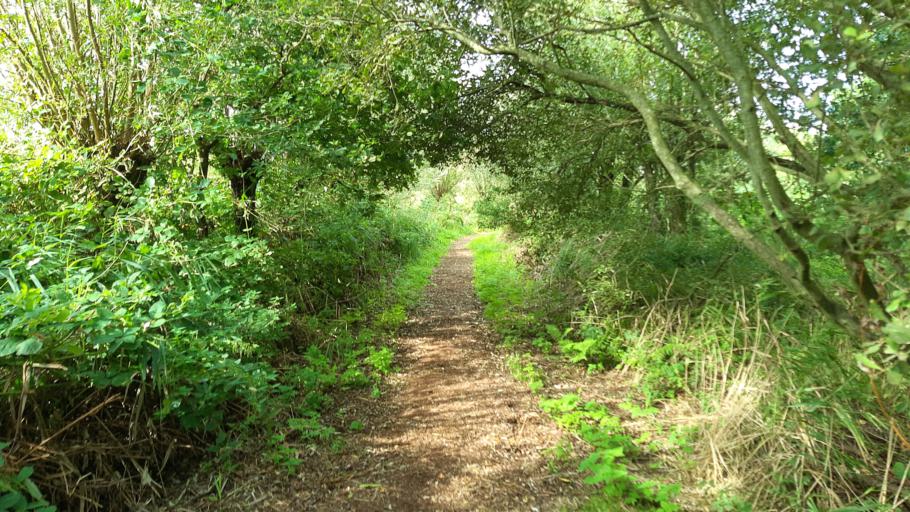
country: NL
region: South Holland
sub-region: Gemeente Pijnacker-Nootdorp
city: Pijnacker
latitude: 51.9779
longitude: 4.4037
